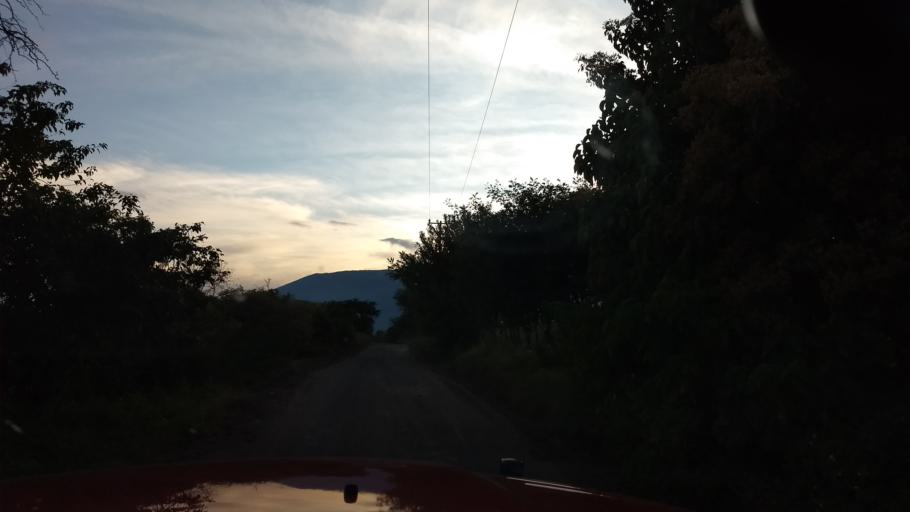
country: MX
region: Colima
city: Suchitlan
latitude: 19.4842
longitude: -103.7960
